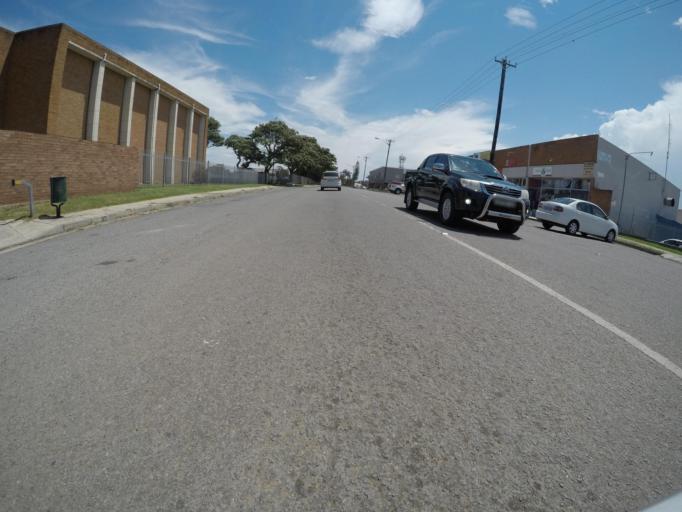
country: ZA
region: Eastern Cape
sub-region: Buffalo City Metropolitan Municipality
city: East London
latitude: -33.0353
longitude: 27.8606
